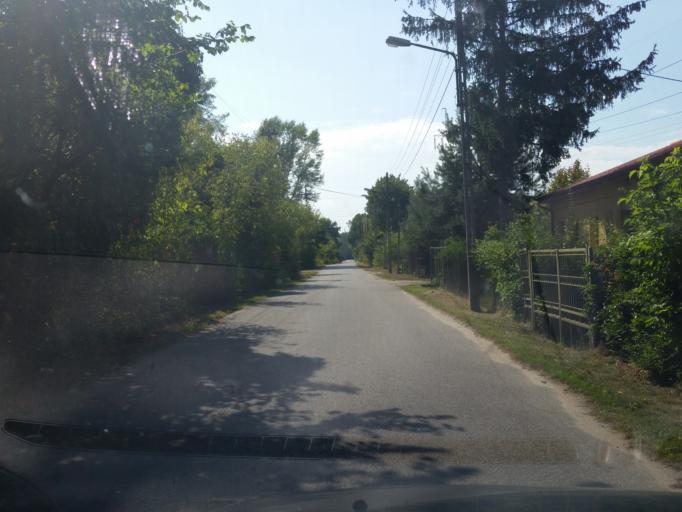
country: PL
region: Masovian Voivodeship
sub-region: Warszawa
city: Bialoleka
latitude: 52.3216
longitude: 20.9883
